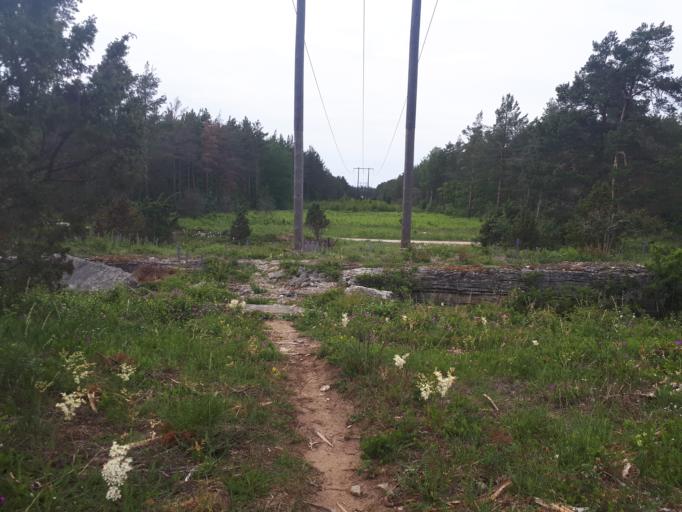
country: SE
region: Gotland
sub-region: Gotland
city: Visby
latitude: 57.6031
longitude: 18.3057
